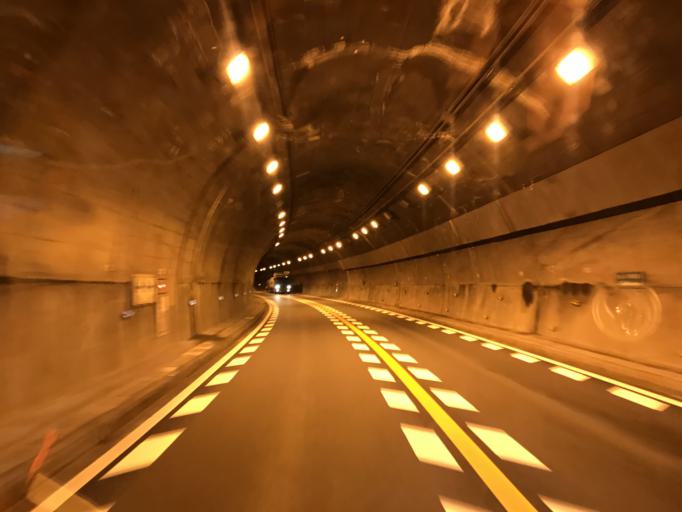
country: JP
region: Shizuoka
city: Gotemba
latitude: 35.3657
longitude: 138.9771
